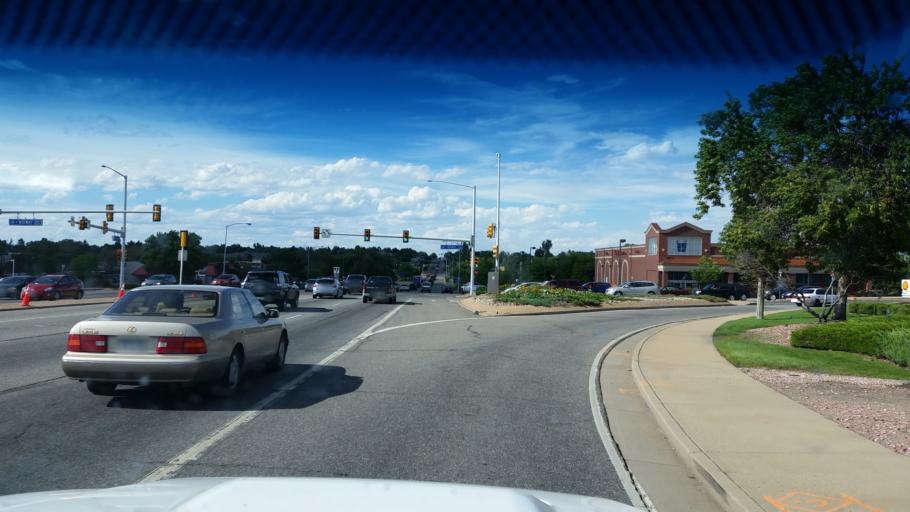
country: US
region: Colorado
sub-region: Broomfield County
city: Broomfield
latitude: 39.9215
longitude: -105.0906
